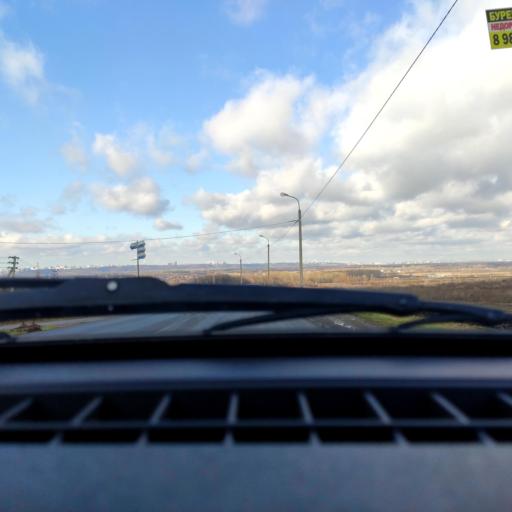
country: RU
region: Bashkortostan
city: Kabakovo
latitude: 54.6360
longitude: 56.0941
